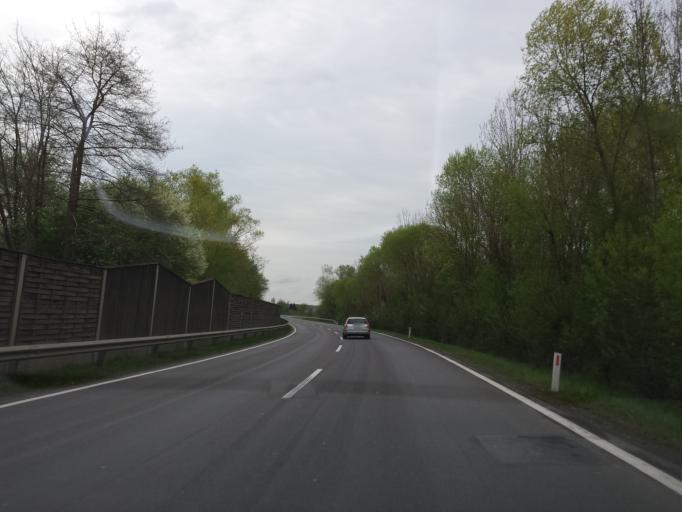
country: AT
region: Styria
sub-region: Politischer Bezirk Hartberg-Fuerstenfeld
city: Altenmarkt bei Fuerstenfeld
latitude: 47.0614
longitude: 16.0507
